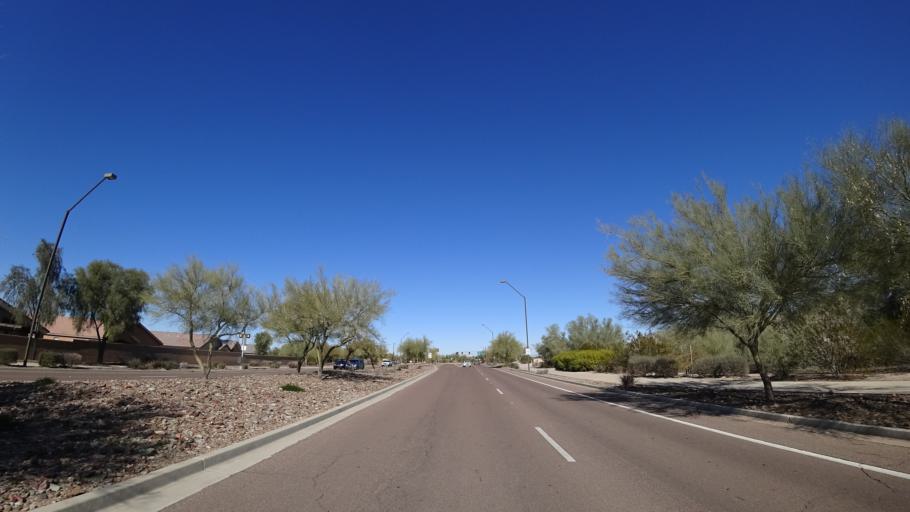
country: US
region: Arizona
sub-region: Maricopa County
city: Goodyear
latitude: 33.3305
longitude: -112.4249
